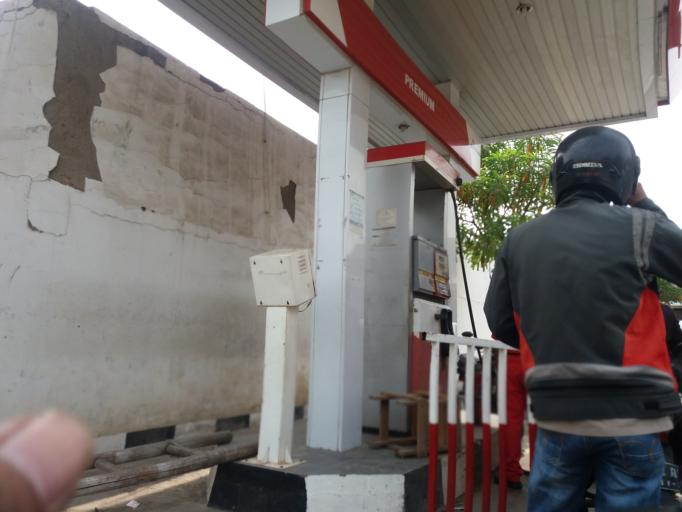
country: ID
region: Jakarta Raya
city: Jakarta
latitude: -6.1341
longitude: 106.8171
